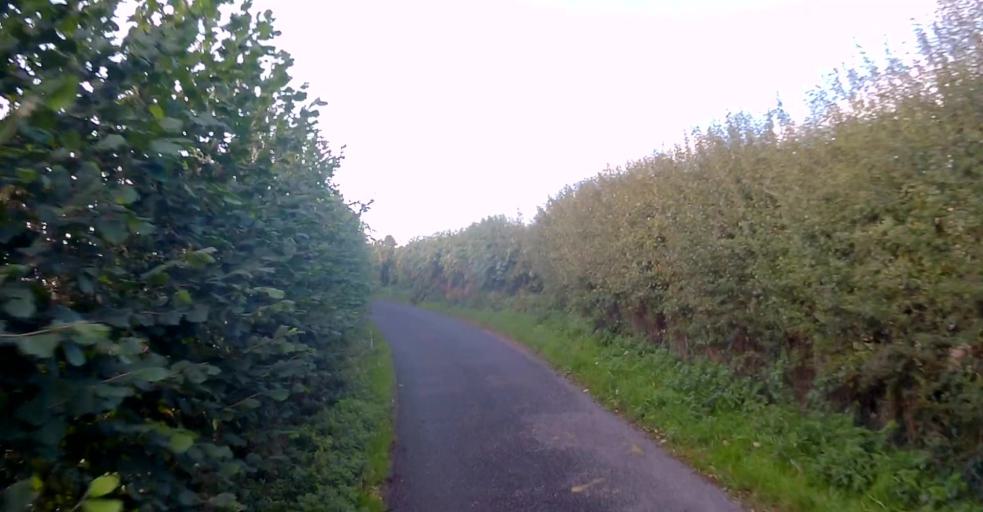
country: GB
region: England
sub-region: Surrey
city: Farnham
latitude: 51.2089
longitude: -0.8509
